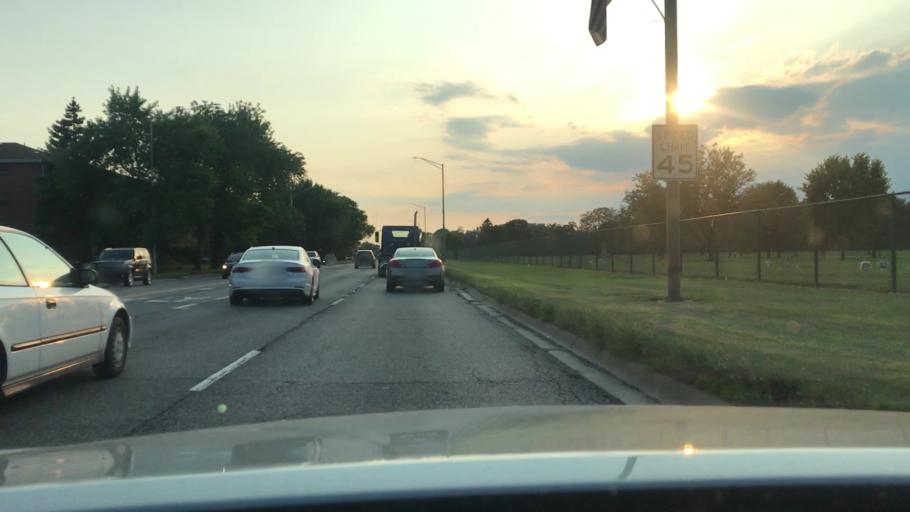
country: US
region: Illinois
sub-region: Cook County
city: Justice
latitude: 41.7476
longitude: -87.8247
